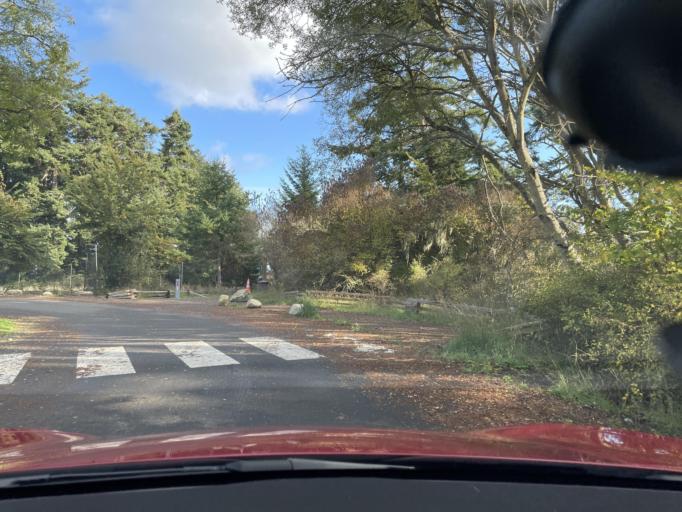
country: US
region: Washington
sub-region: San Juan County
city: Friday Harbor
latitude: 48.4643
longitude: -123.0242
